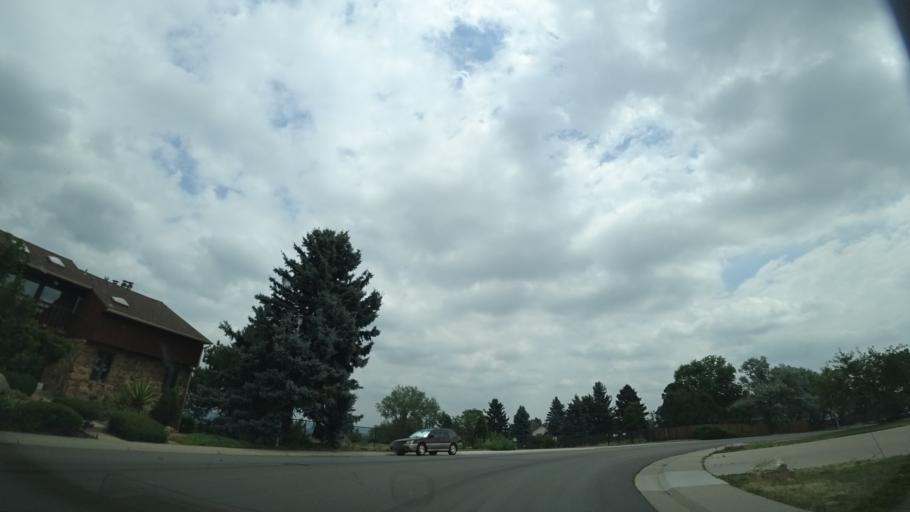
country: US
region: Colorado
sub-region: Jefferson County
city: West Pleasant View
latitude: 39.7163
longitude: -105.1557
